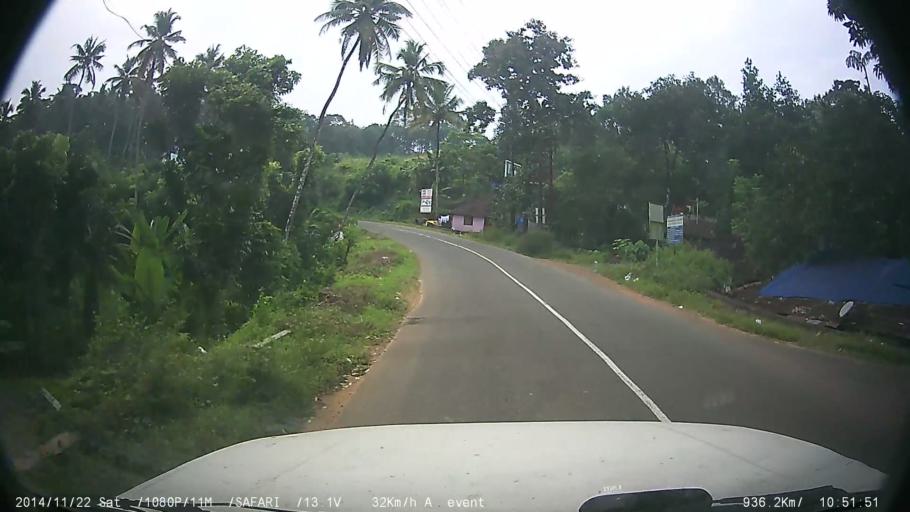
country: IN
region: Kerala
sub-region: Ernakulam
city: Muvattupuzha
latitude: 9.9676
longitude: 76.5783
